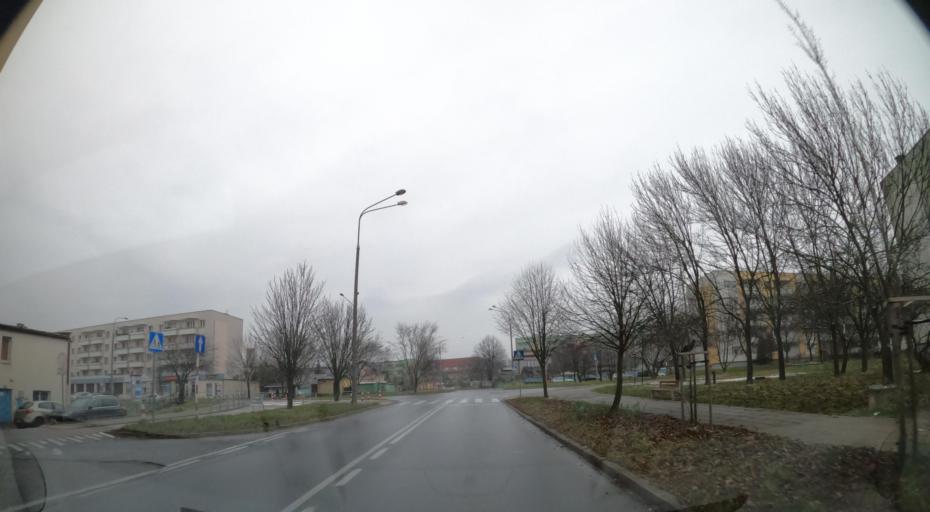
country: PL
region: Masovian Voivodeship
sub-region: Powiat radomski
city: Trablice
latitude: 51.3708
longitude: 21.1345
